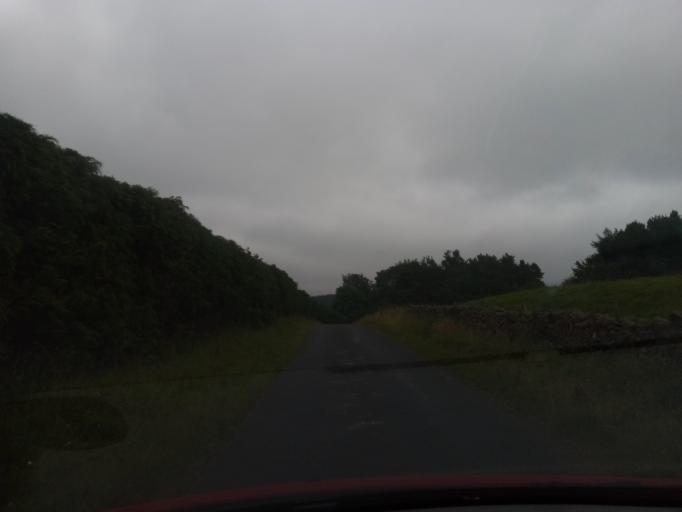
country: GB
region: Scotland
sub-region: Fife
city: Pathhead
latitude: 55.7575
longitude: -2.9318
